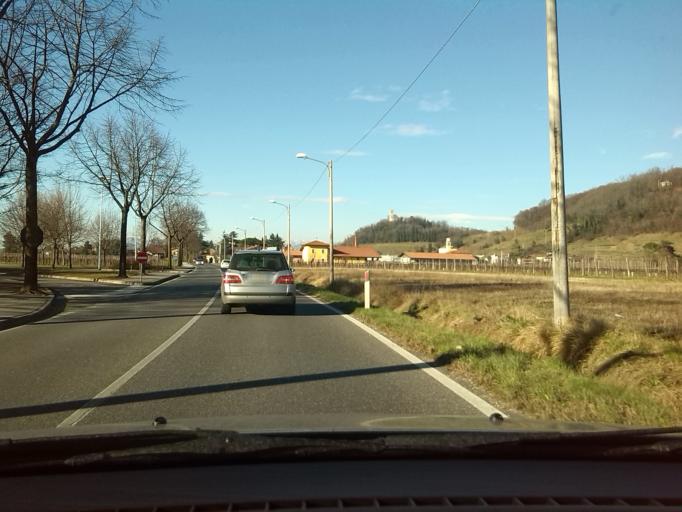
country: IT
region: Friuli Venezia Giulia
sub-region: Provincia di Gorizia
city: Cormons
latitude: 45.9683
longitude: 13.4589
